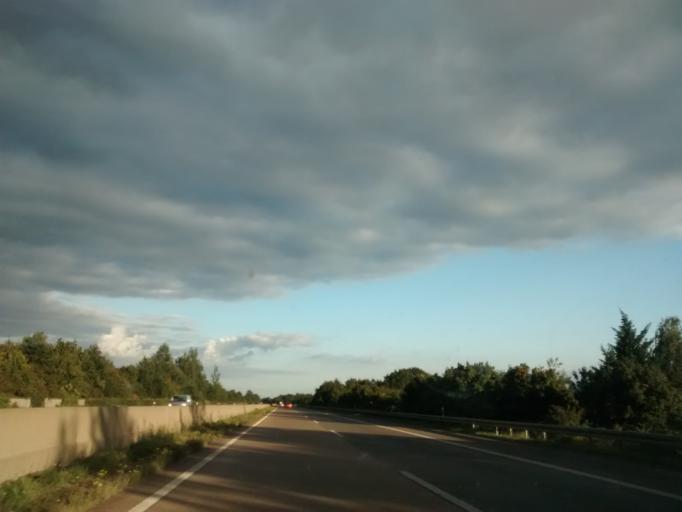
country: DE
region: North Rhine-Westphalia
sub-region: Regierungsbezirk Munster
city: Dreierwalde
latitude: 52.2980
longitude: 7.5055
